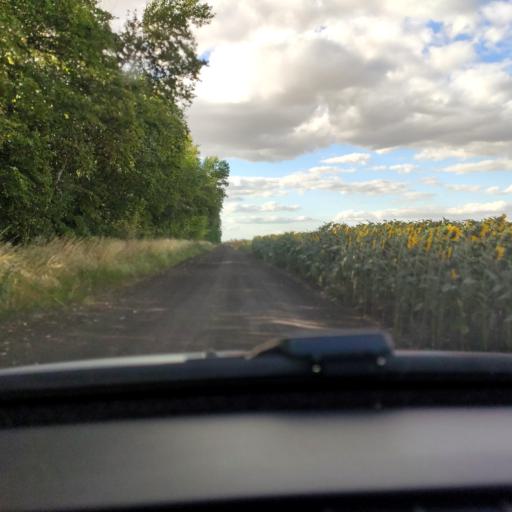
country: RU
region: Voronezj
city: Verkhnyaya Khava
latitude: 51.5952
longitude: 39.8417
